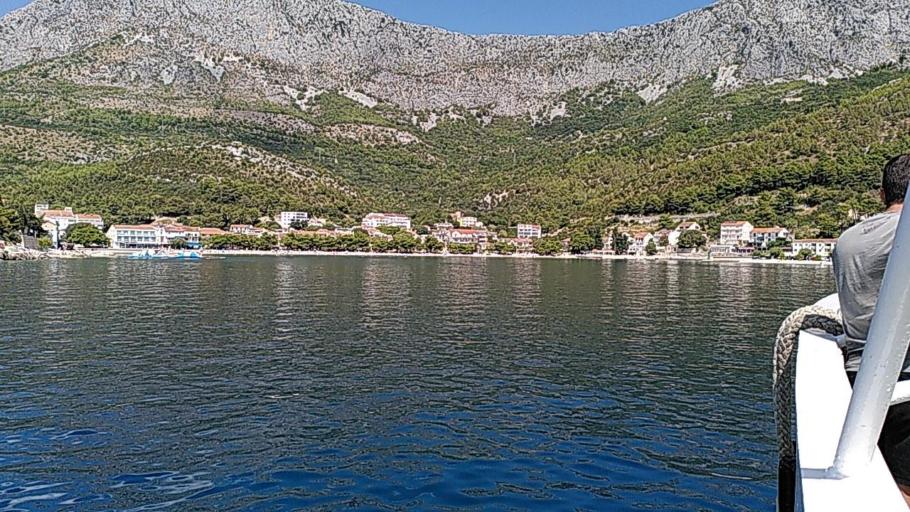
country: HR
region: Splitsko-Dalmatinska
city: Vrgorac
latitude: 43.1518
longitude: 17.2460
